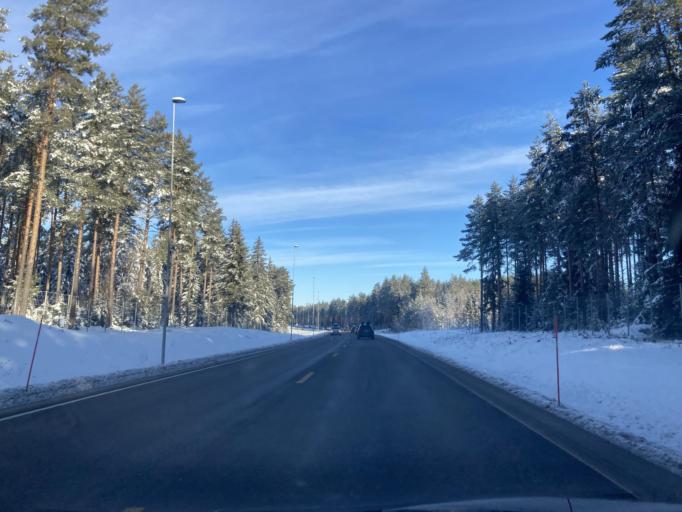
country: NO
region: Hedmark
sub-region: Loten
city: Loten
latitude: 60.7625
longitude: 11.3087
